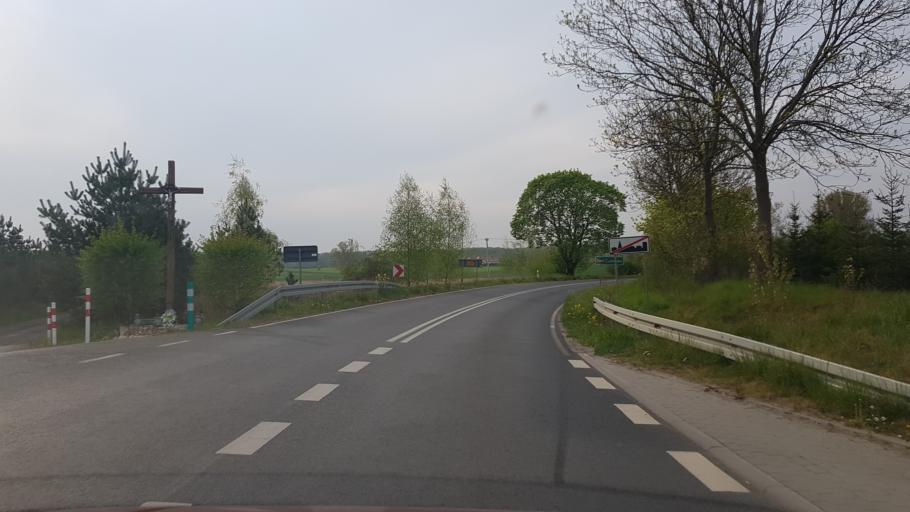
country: PL
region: West Pomeranian Voivodeship
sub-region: Powiat gryfinski
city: Stare Czarnowo
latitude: 53.2792
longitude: 14.7733
